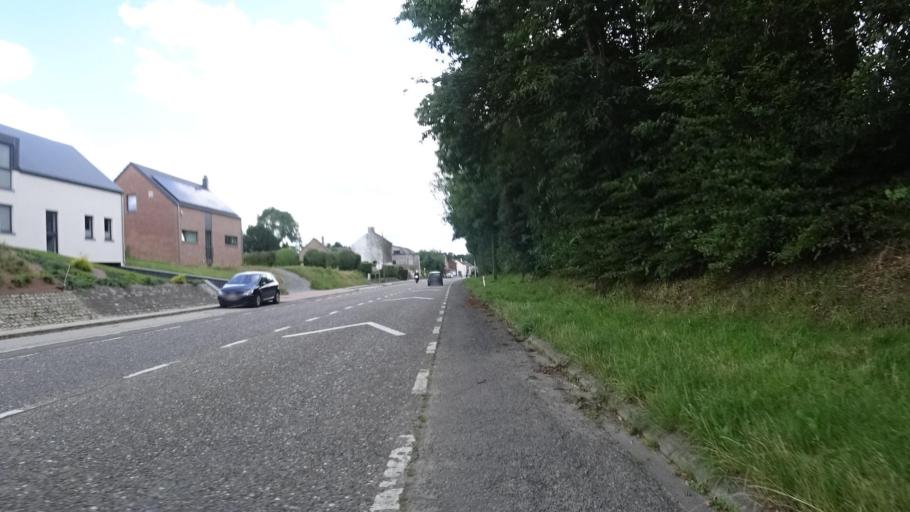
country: BE
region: Wallonia
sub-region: Province du Brabant Wallon
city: Villers-la-Ville
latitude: 50.5485
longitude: 4.5339
